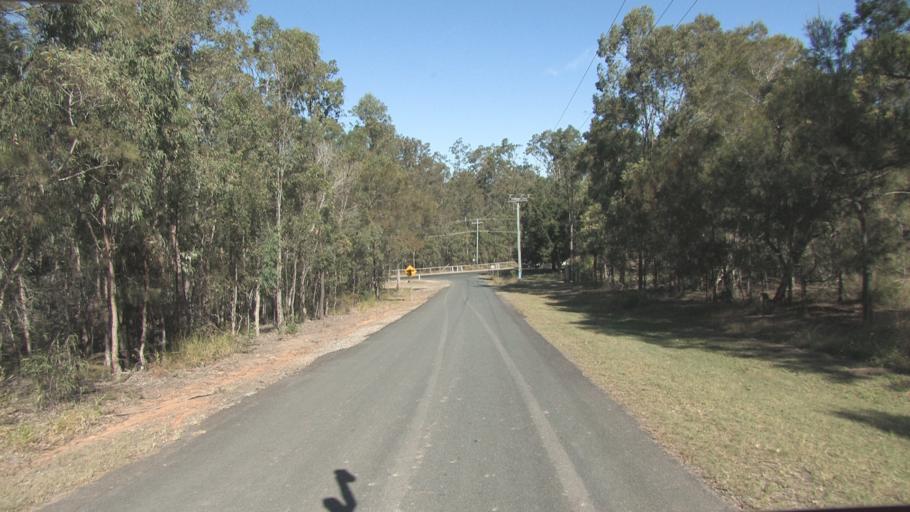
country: AU
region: Queensland
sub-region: Ipswich
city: Springfield Lakes
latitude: -27.7047
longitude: 152.9689
